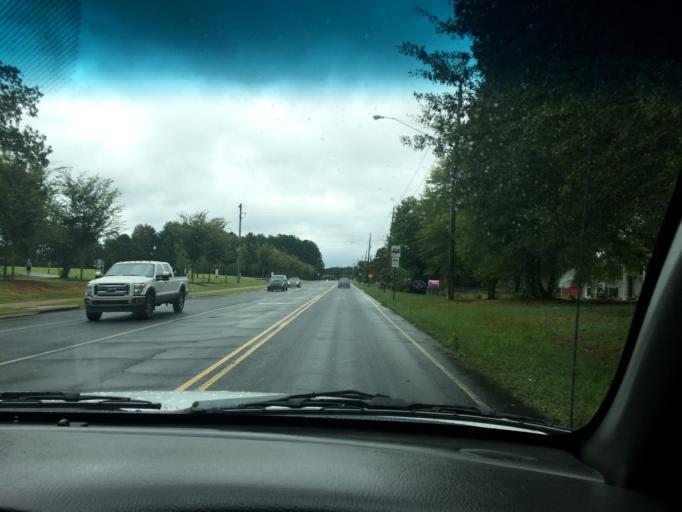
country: US
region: Georgia
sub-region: Cobb County
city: Kennesaw
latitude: 34.0310
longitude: -84.6327
